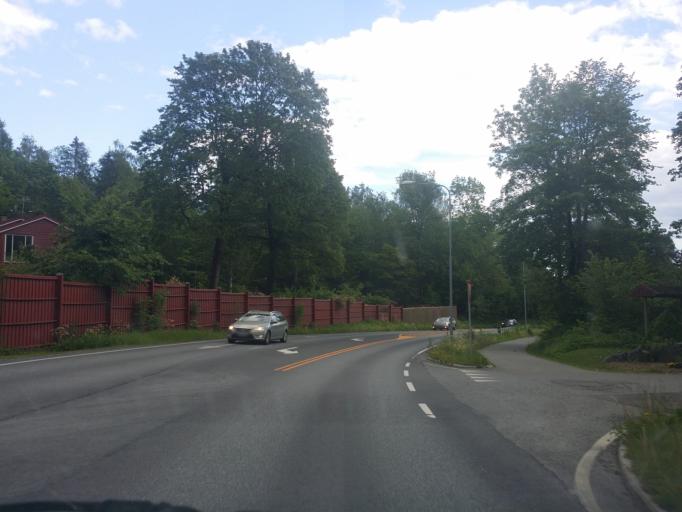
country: NO
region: Akershus
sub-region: Baerum
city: Sandvika
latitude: 59.9295
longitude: 10.5537
